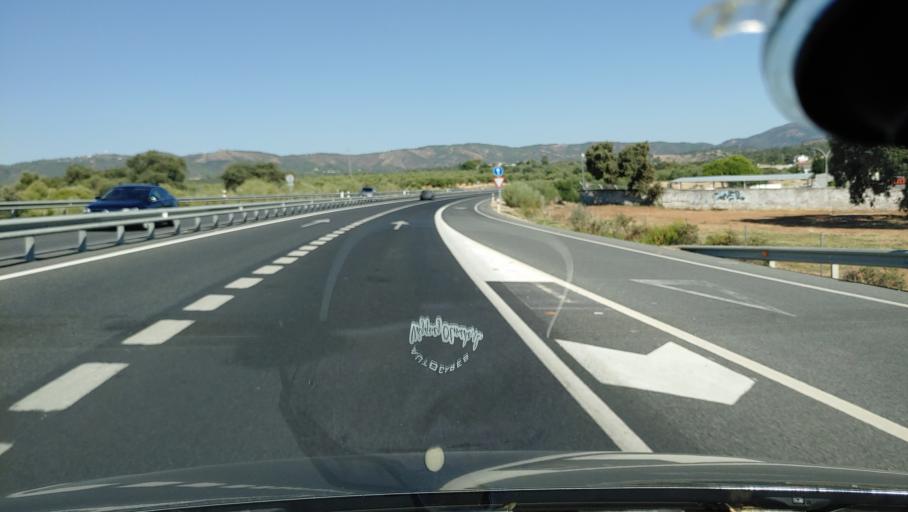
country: ES
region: Andalusia
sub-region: Province of Cordoba
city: Cordoba
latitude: 37.9203
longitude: -4.7634
